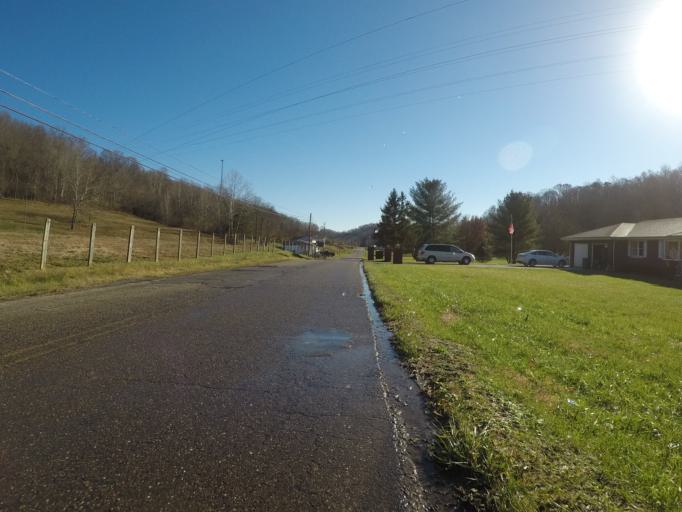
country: US
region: West Virginia
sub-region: Cabell County
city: Huntington
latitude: 38.4822
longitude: -82.4785
